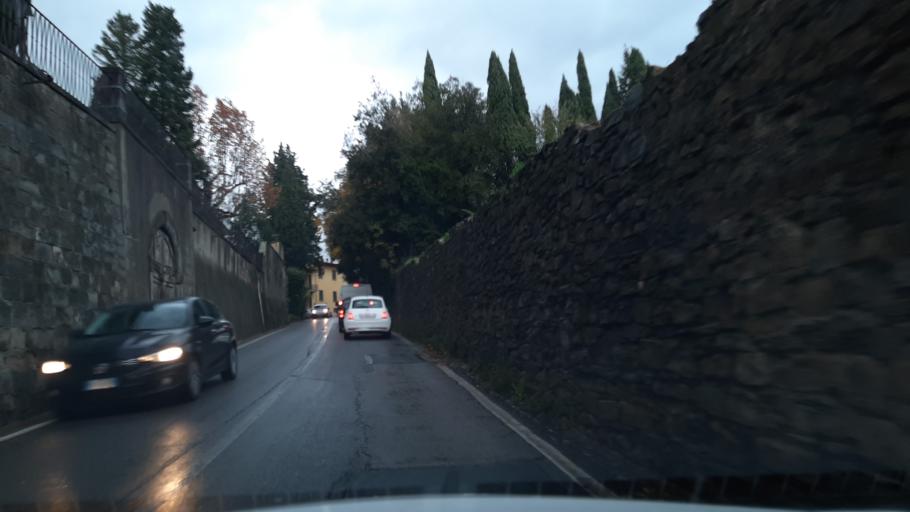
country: IT
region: Tuscany
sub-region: Province of Florence
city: Fiesole
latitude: 43.8023
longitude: 11.2681
